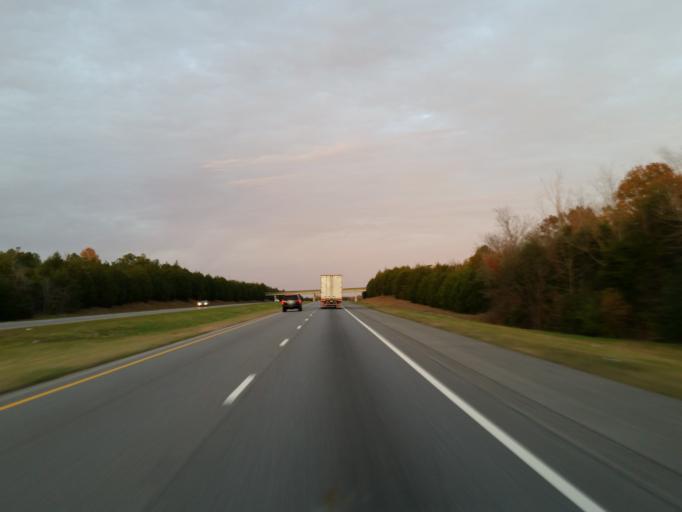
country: US
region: Alabama
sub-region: Sumter County
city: Livingston
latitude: 32.6769
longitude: -88.1671
